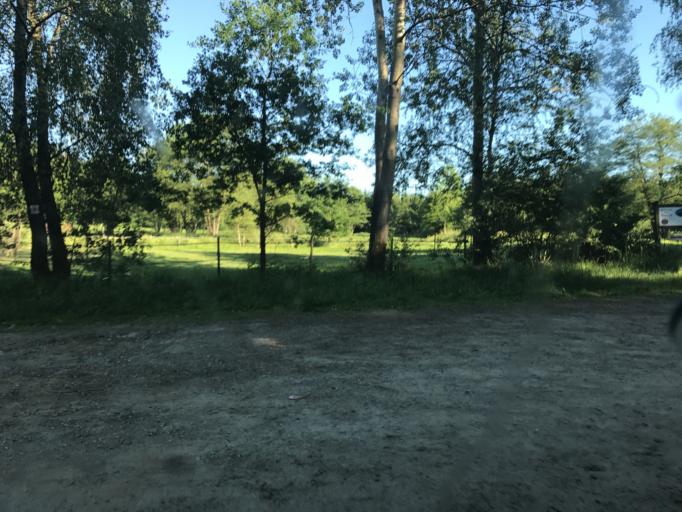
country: DE
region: Bavaria
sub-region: Upper Palatinate
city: Waldmunchen
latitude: 49.3872
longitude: 12.7227
